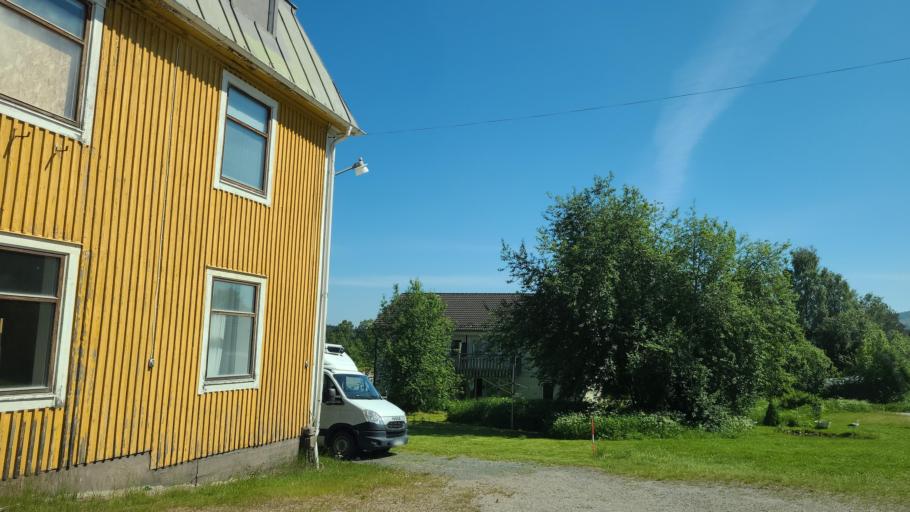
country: SE
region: Vaesterbotten
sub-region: Bjurholms Kommun
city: Bjurholm
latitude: 63.6930
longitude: 18.8656
